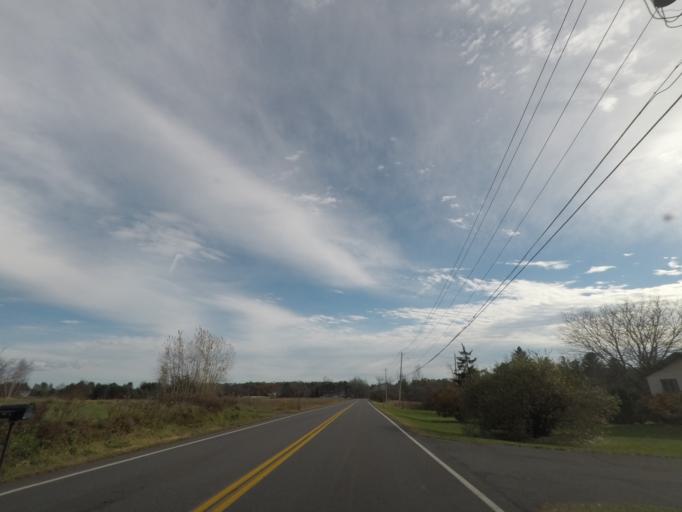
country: US
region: New York
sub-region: Albany County
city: Voorheesville
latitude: 42.6278
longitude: -73.9063
